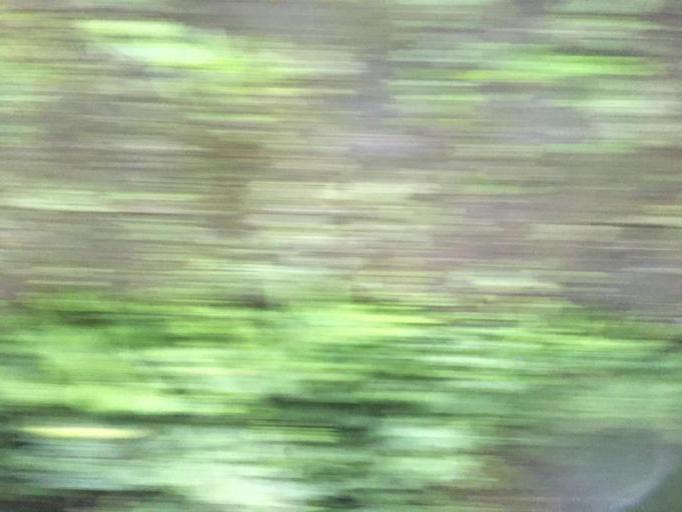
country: TW
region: Taiwan
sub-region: Yilan
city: Yilan
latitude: 24.5504
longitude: 121.5083
